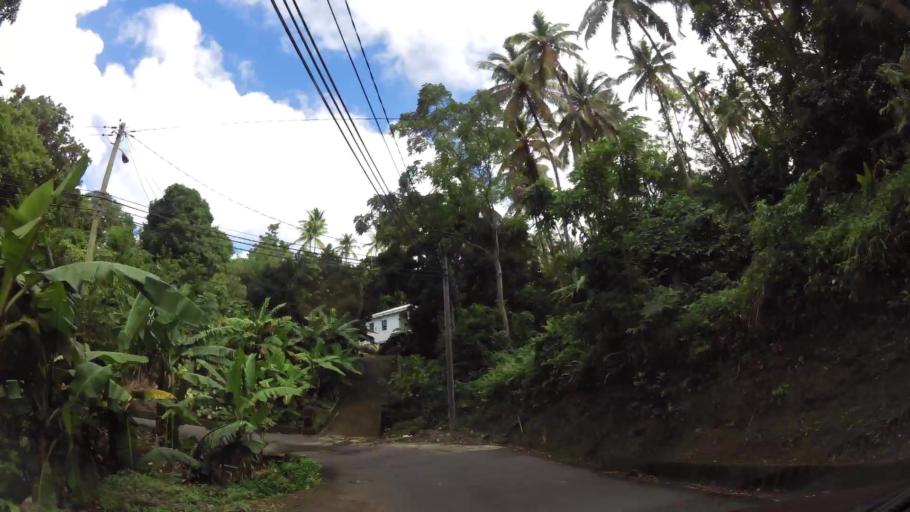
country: DM
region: Saint John
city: Portsmouth
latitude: 15.6152
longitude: -61.4630
